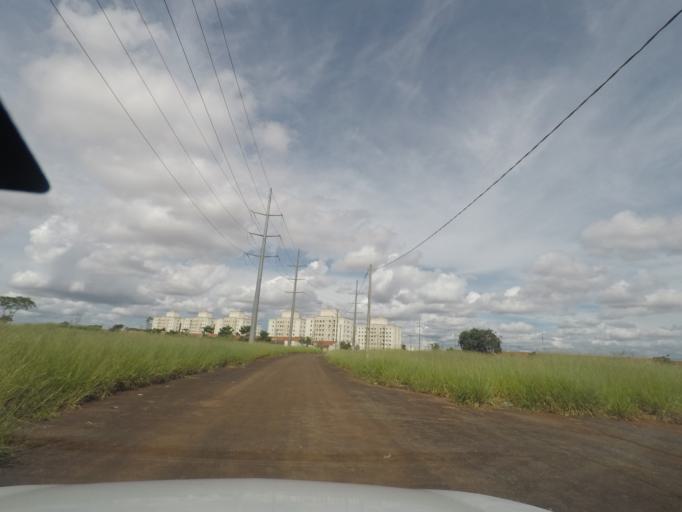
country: BR
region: Goias
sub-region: Goiania
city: Goiania
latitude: -16.7158
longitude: -49.3484
